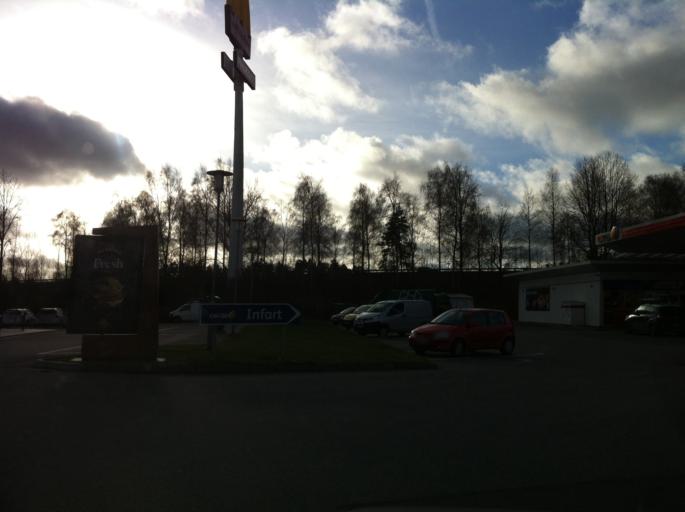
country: SE
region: Kronoberg
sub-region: Vaxjo Kommun
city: Vaexjoe
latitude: 56.8551
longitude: 14.7302
